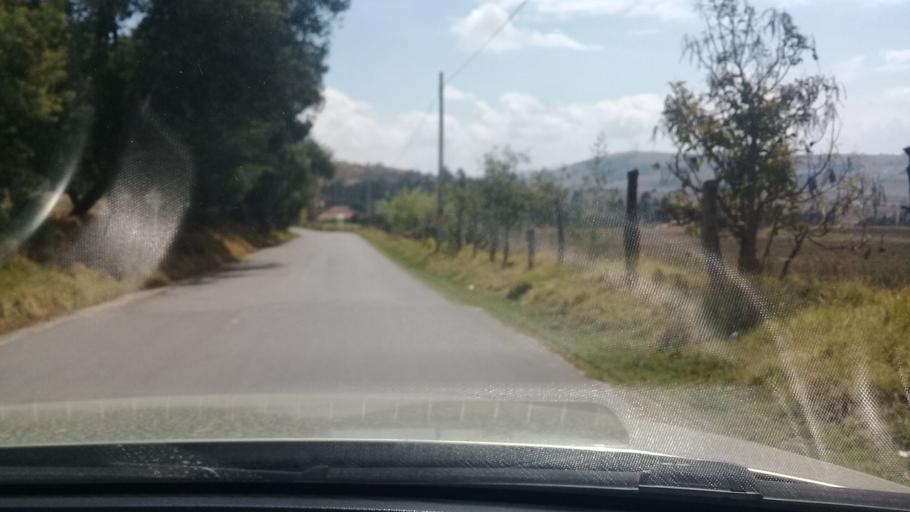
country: CO
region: Boyaca
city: Siachoque
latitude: 5.5551
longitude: -73.2852
